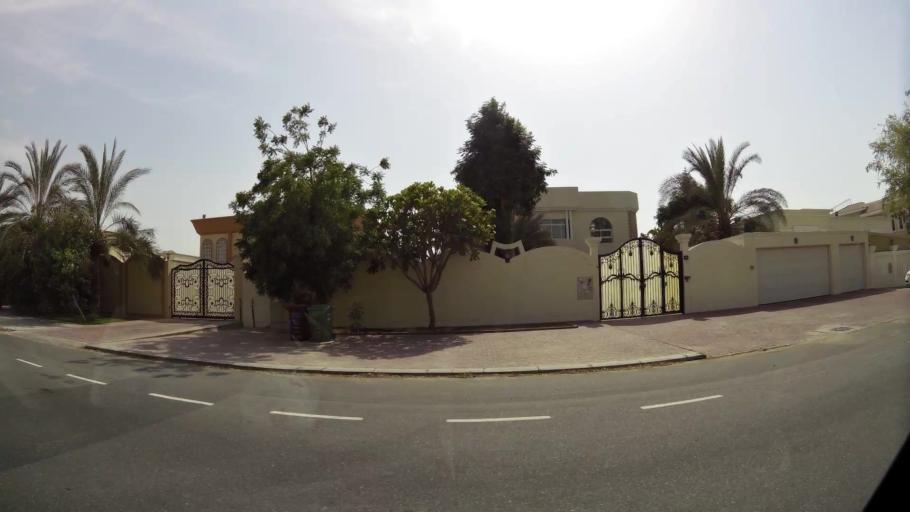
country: AE
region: Ash Shariqah
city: Sharjah
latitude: 25.2534
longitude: 55.4344
